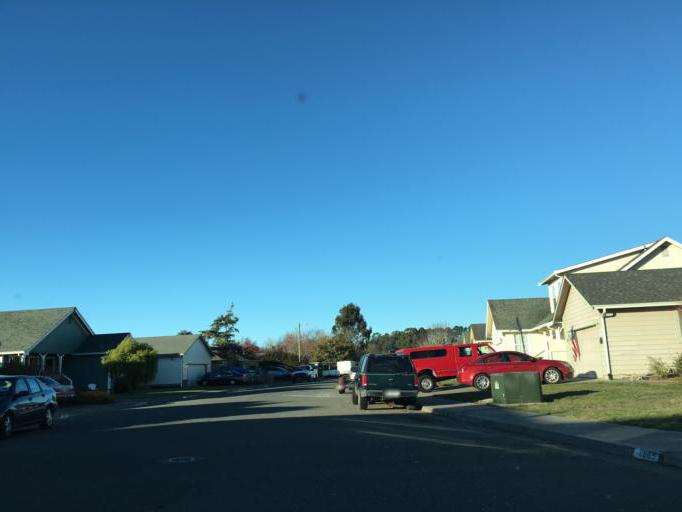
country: US
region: California
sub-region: Humboldt County
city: McKinleyville
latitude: 40.9586
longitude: -124.1050
